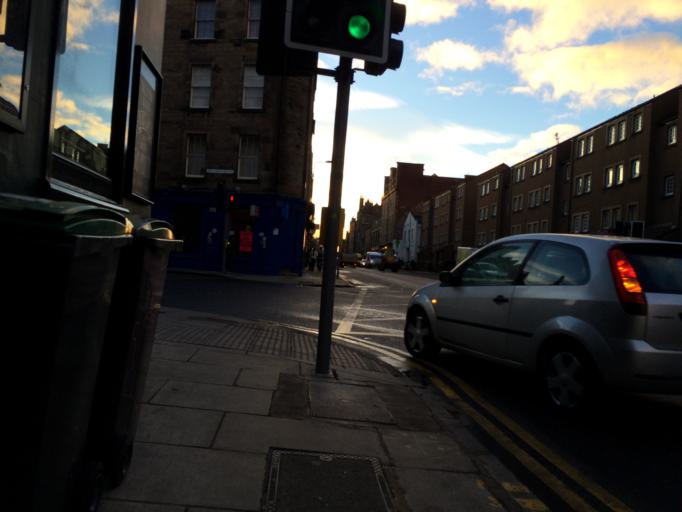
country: GB
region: Scotland
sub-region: Edinburgh
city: Edinburgh
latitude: 55.9391
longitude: -3.1819
